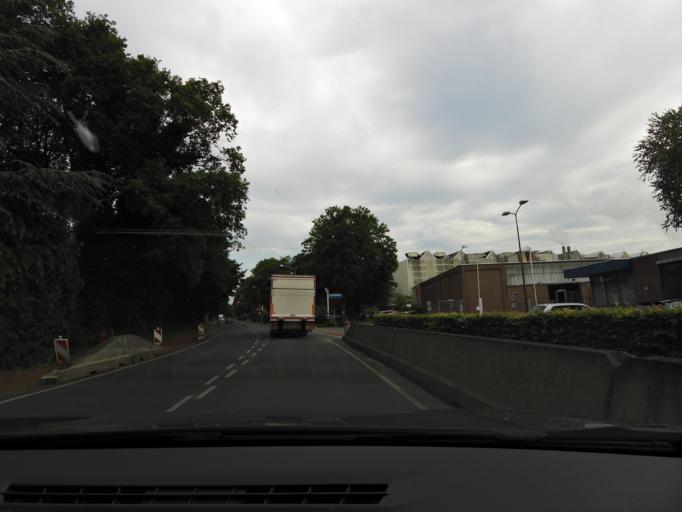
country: NL
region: Gelderland
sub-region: Gemeente Brummen
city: Eerbeek
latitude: 52.0968
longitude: 6.0532
